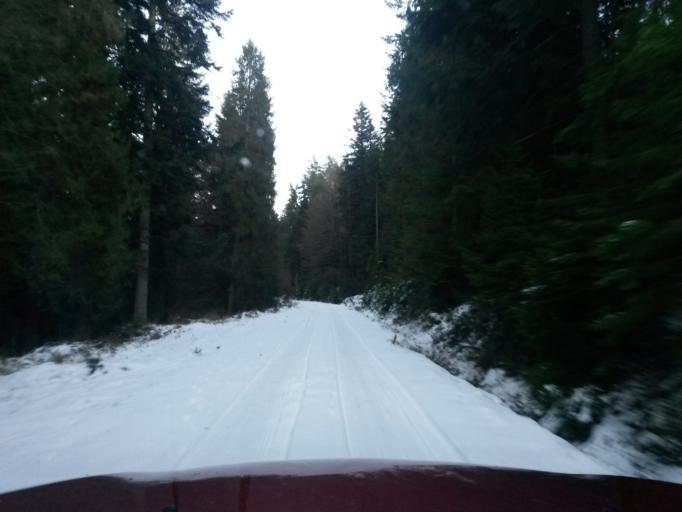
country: SK
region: Kosicky
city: Medzev
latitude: 48.7839
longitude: 20.8110
